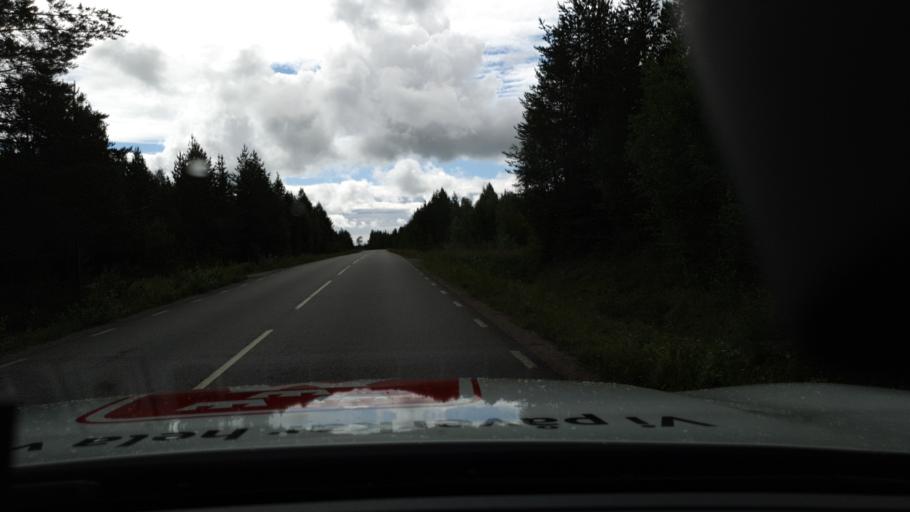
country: SE
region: Norrbotten
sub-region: Lulea Kommun
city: Sodra Sunderbyn
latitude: 65.5027
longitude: 21.8695
